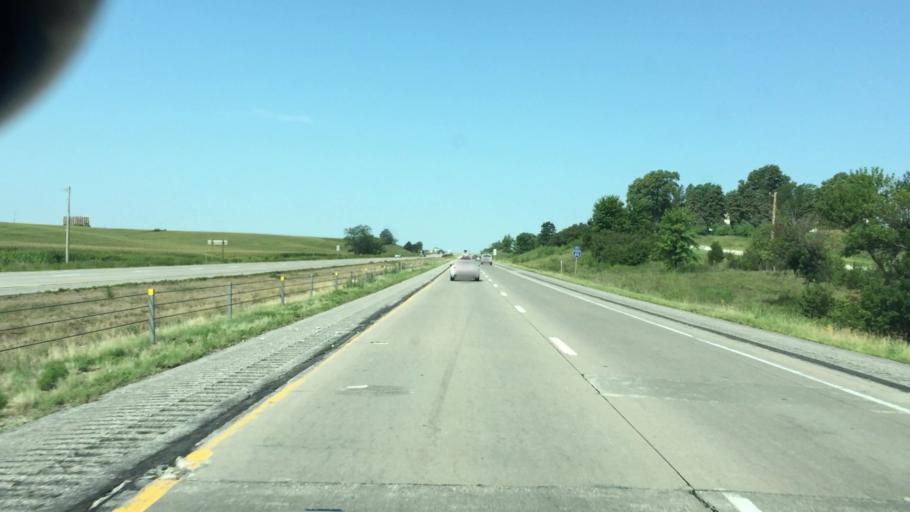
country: US
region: Iowa
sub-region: Iowa County
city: Williamsburg
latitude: 41.6872
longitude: -92.0161
